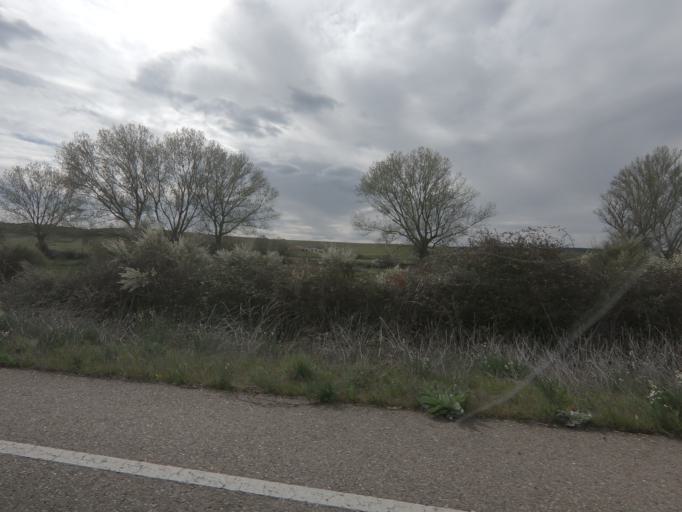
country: ES
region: Castille and Leon
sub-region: Provincia de Salamanca
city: Pastores
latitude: 40.5262
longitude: -6.5672
